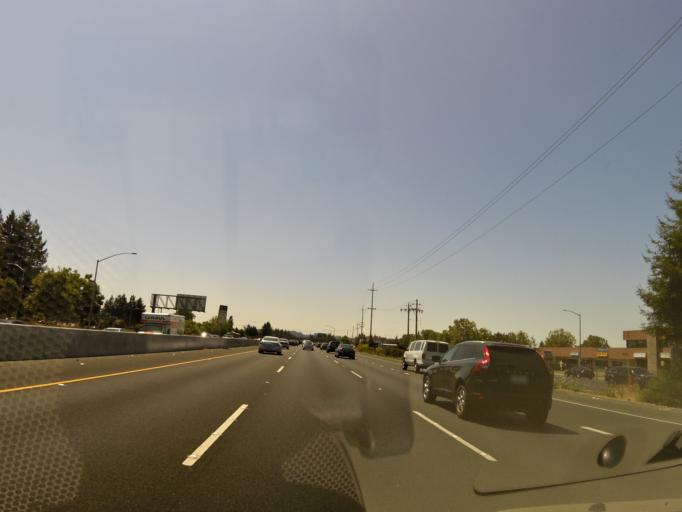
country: US
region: California
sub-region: Sonoma County
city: Rohnert Park
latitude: 38.3562
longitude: -122.7131
